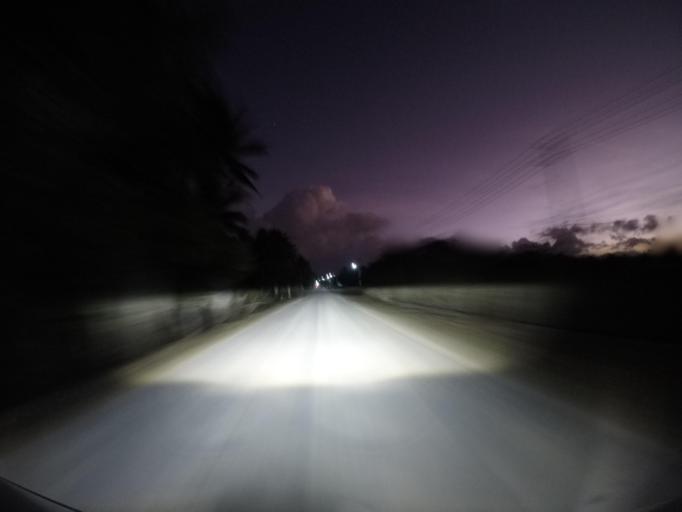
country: TL
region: Lautem
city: Lospalos
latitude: -8.4637
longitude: 126.9963
